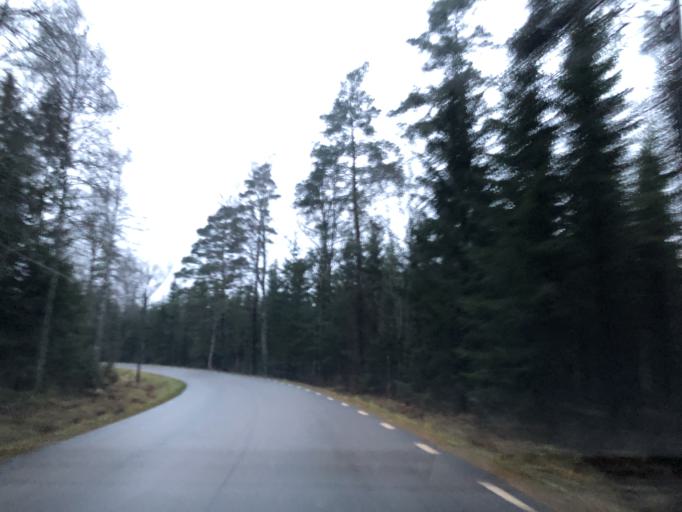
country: SE
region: Vaestra Goetaland
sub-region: Ulricehamns Kommun
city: Ulricehamn
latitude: 57.8515
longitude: 13.2563
